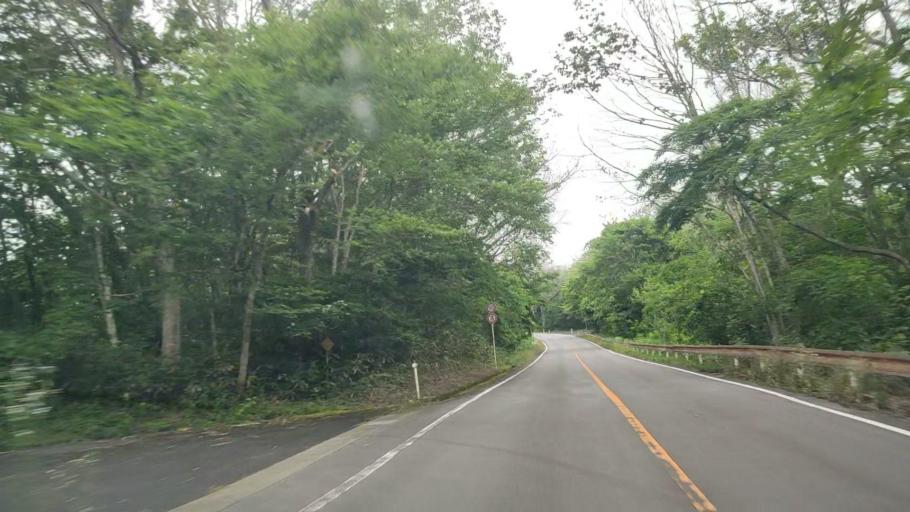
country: JP
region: Tottori
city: Kurayoshi
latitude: 35.3088
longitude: 133.6152
